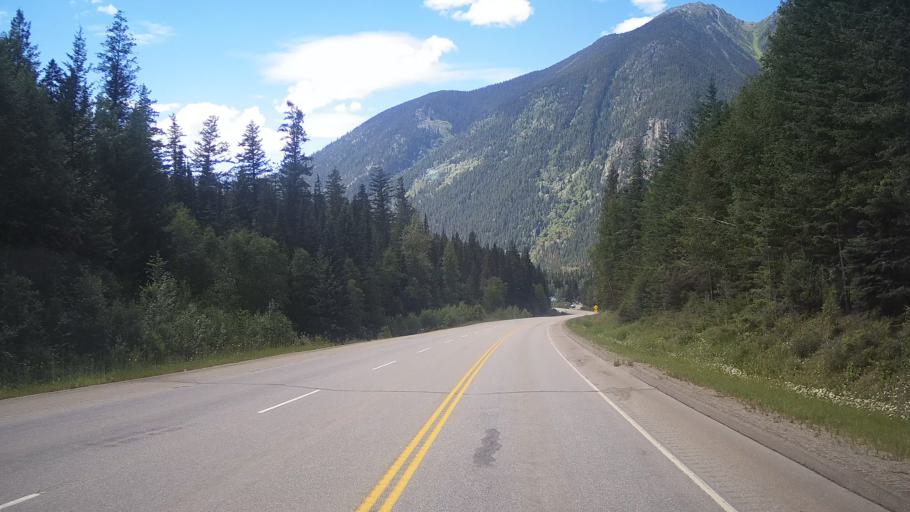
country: CA
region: Alberta
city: Grande Cache
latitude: 53.0326
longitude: -119.2182
